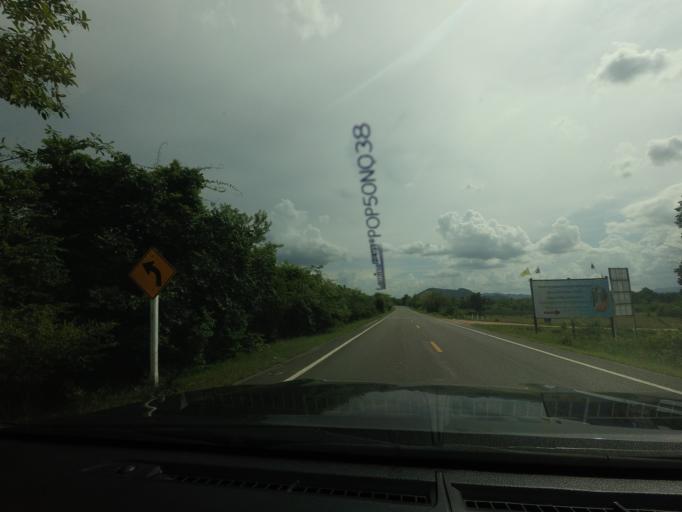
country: TH
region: Kanchanaburi
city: Bo Phloi
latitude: 14.1605
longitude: 99.4287
